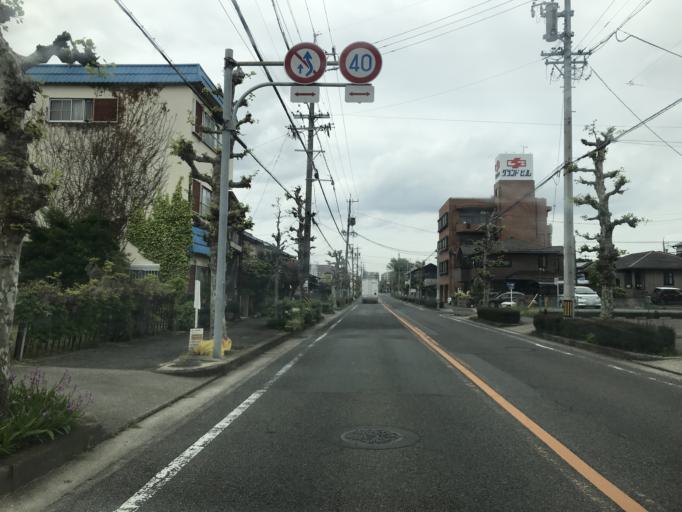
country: JP
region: Aichi
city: Kasugai
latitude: 35.2407
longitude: 136.9756
